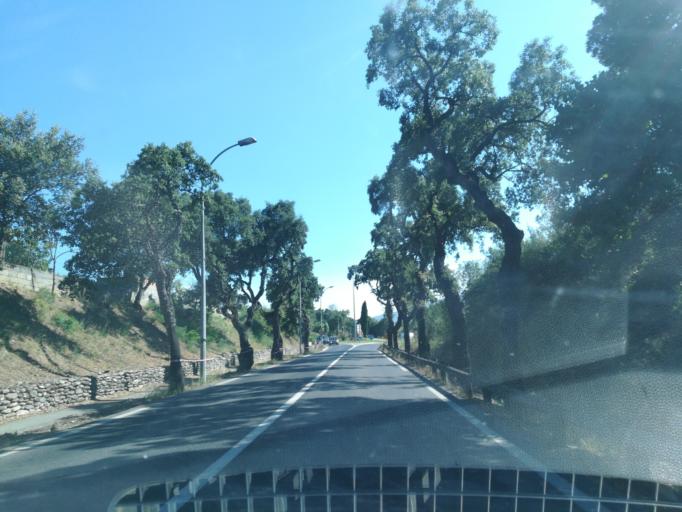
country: FR
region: Languedoc-Roussillon
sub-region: Departement des Pyrenees-Orientales
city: el Volo
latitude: 42.5151
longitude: 2.8307
